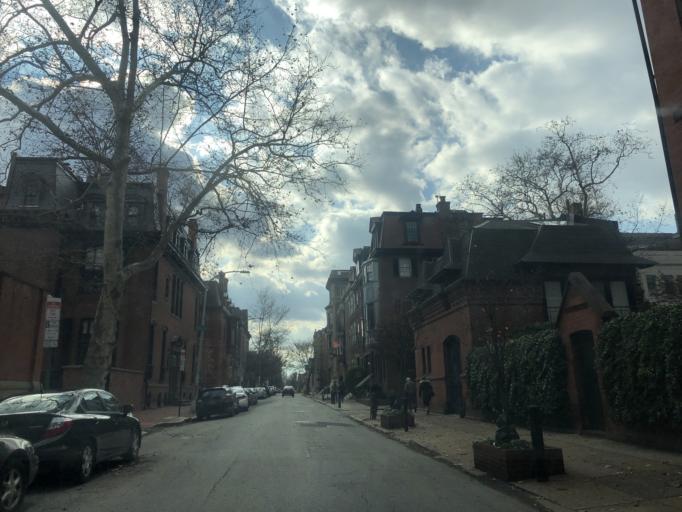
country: US
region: Pennsylvania
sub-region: Philadelphia County
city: Philadelphia
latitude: 39.9483
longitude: -75.1763
